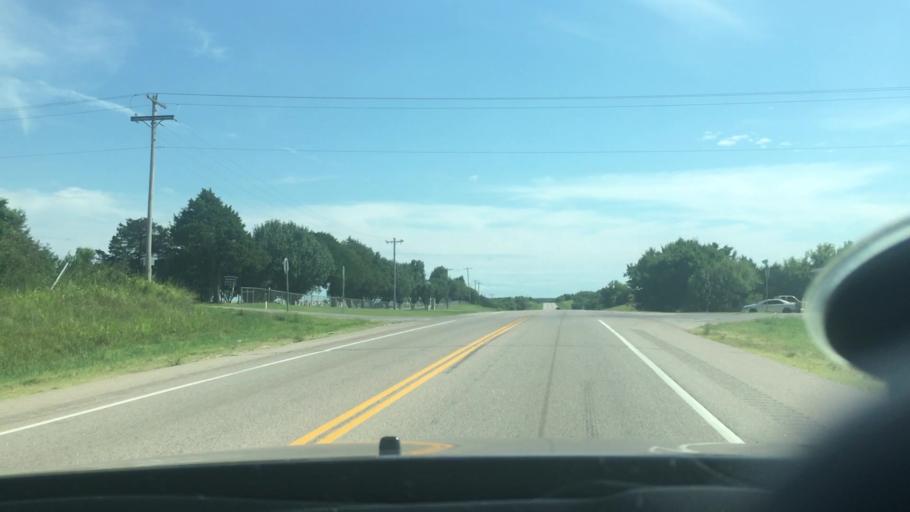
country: US
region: Oklahoma
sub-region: Seminole County
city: Konawa
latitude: 34.9859
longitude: -96.6794
